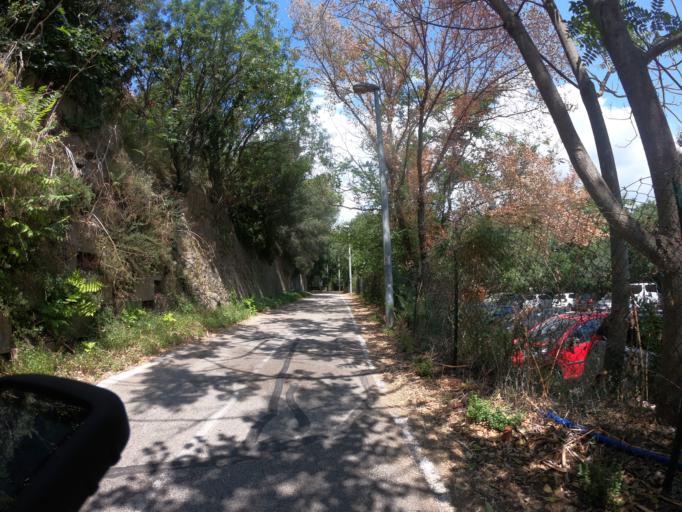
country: FR
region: Provence-Alpes-Cote d'Azur
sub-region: Departement du Var
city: La Valette-du-Var
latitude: 43.1225
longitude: 5.9631
